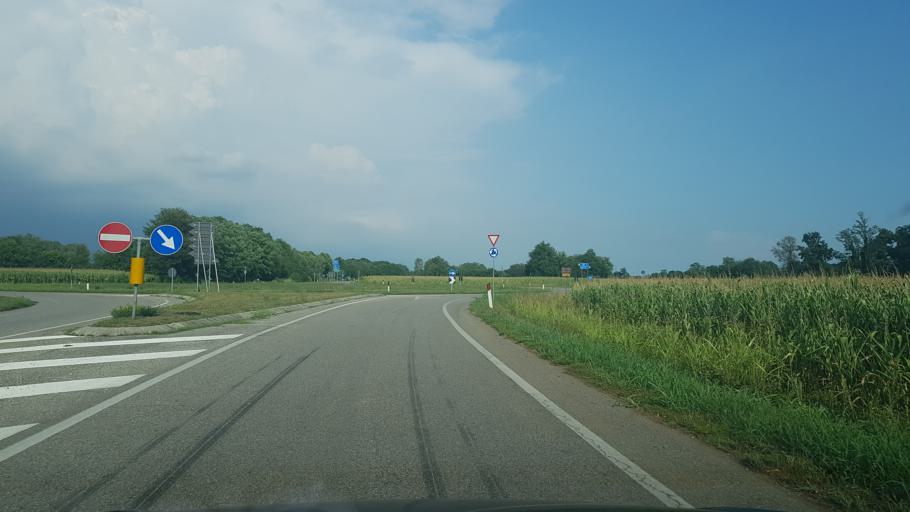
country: IT
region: Friuli Venezia Giulia
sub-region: Provincia di Udine
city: Colloredo di Prato
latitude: 46.0576
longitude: 13.1150
